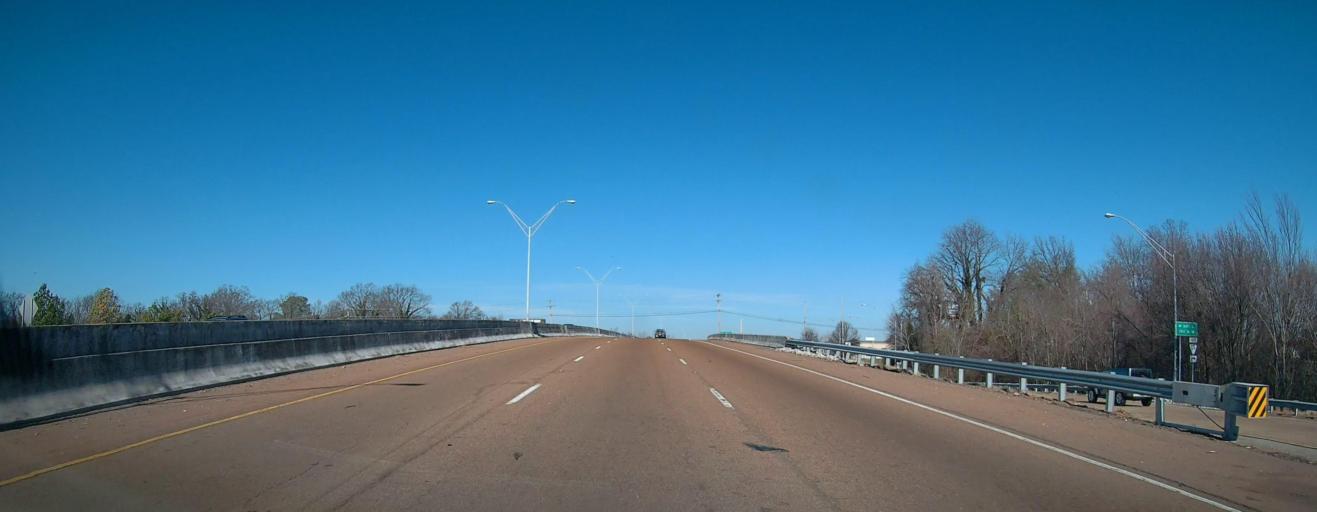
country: US
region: Tennessee
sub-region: Shelby County
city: Bartlett
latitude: 35.2036
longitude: -89.9238
